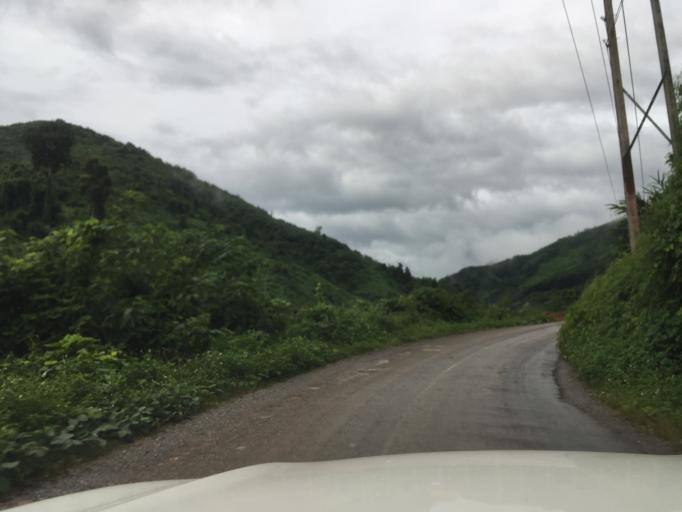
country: LA
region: Oudomxai
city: Muang La
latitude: 21.0265
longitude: 102.2350
